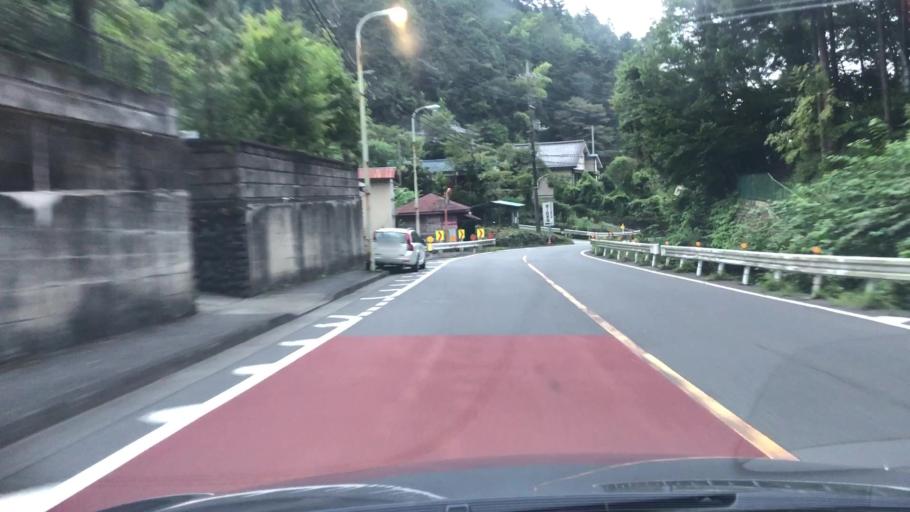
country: JP
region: Tokyo
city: Ome
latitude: 35.7648
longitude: 139.2274
